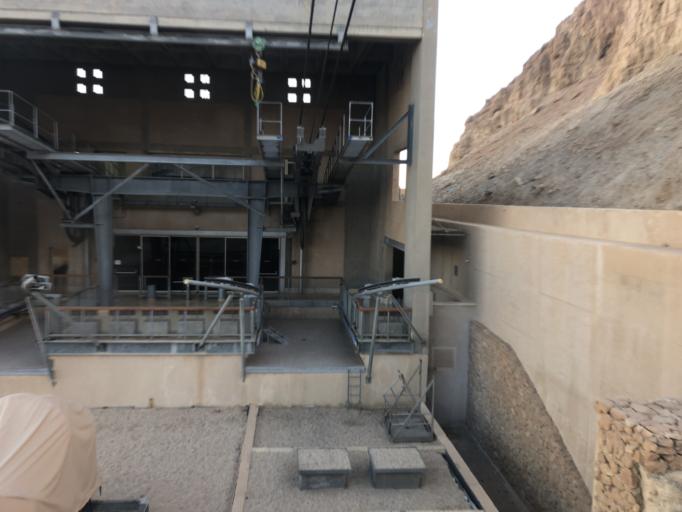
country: IL
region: Southern District
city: `En Boqeq
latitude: 31.3125
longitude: 35.3614
